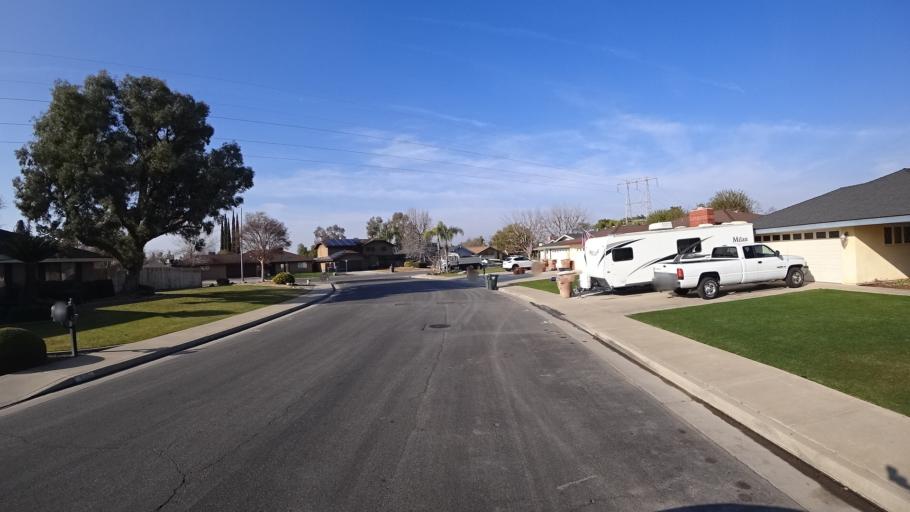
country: US
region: California
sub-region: Kern County
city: Oildale
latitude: 35.4061
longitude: -118.9284
